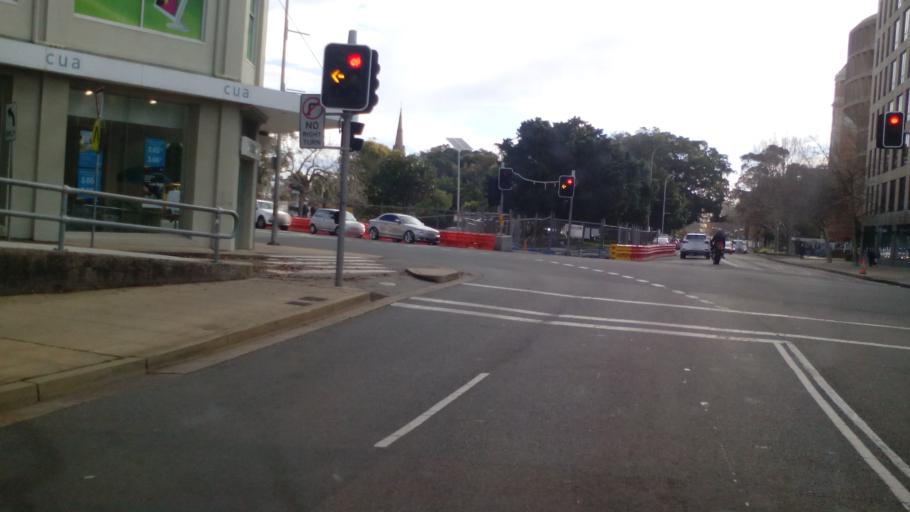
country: AU
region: New South Wales
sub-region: Newcastle
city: Newcastle
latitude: -32.9279
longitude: 151.7744
